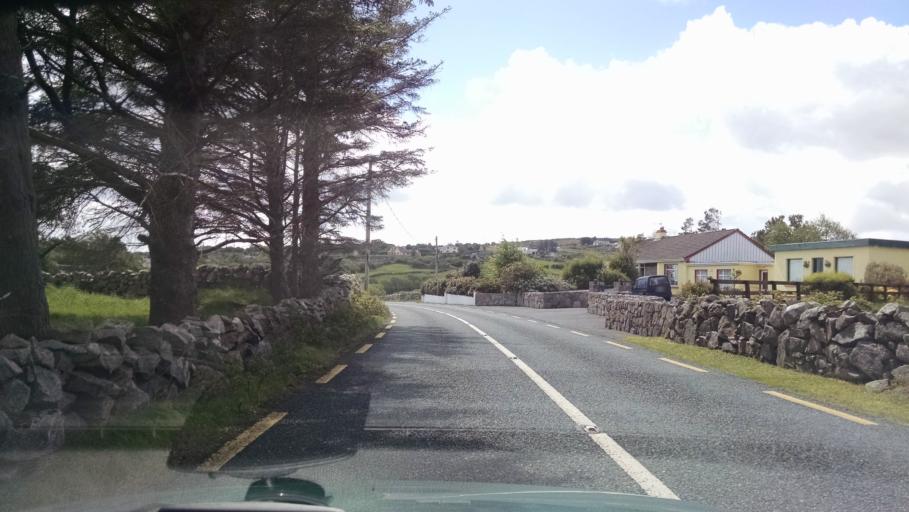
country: IE
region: Connaught
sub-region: County Galway
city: Clifden
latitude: 53.3585
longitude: -9.7037
